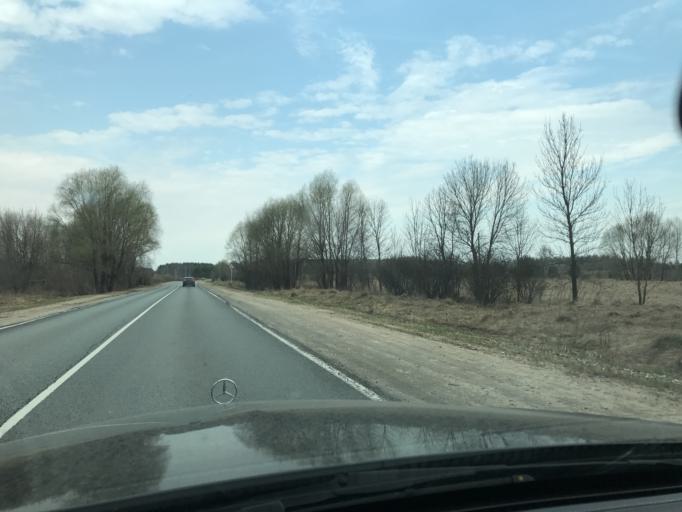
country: RU
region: Vladimir
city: Murom
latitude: 55.6264
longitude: 41.8878
